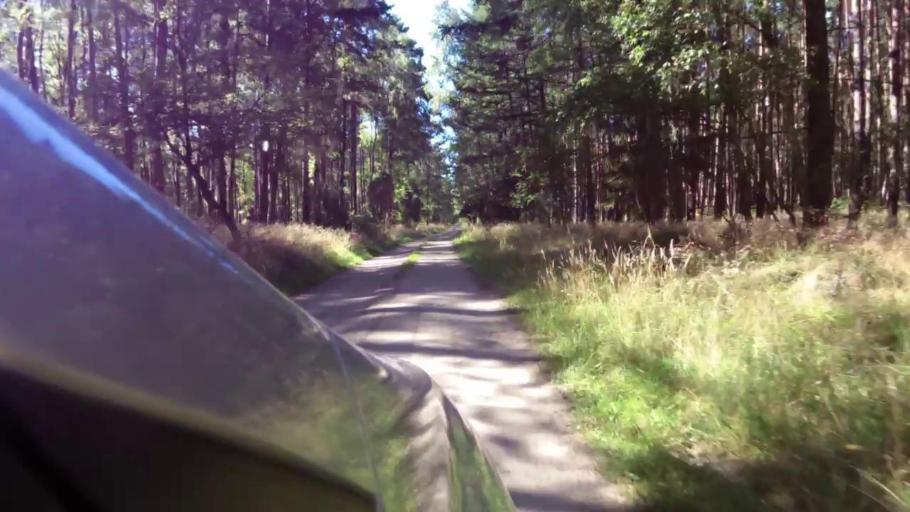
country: PL
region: West Pomeranian Voivodeship
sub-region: Powiat szczecinecki
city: Szczecinek
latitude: 53.8266
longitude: 16.7302
